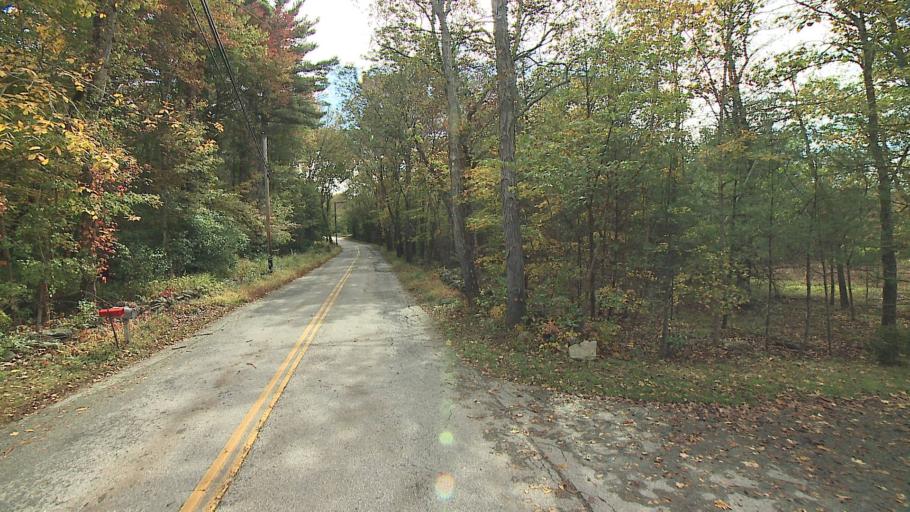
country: US
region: Connecticut
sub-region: Windham County
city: Thompson
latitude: 41.9213
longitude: -71.8208
